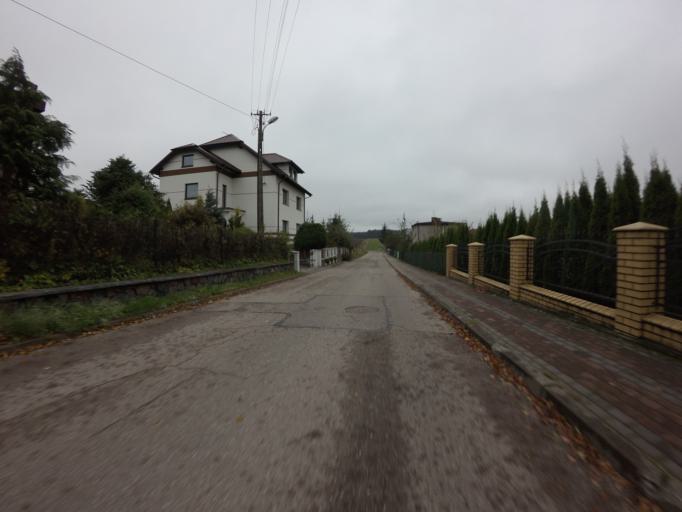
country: PL
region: Pomeranian Voivodeship
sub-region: Powiat kartuski
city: Stezyca
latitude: 54.1673
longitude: 17.9667
